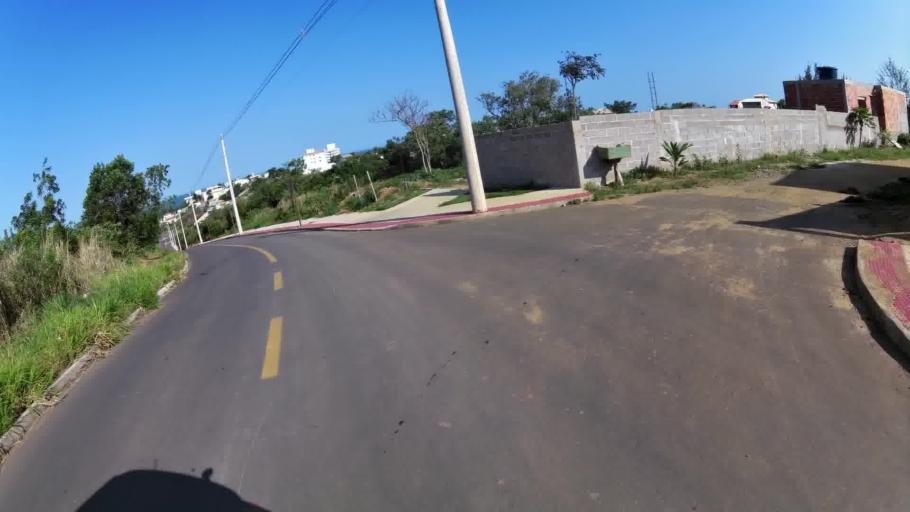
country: BR
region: Espirito Santo
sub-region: Guarapari
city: Guarapari
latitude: -20.7189
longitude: -40.5310
